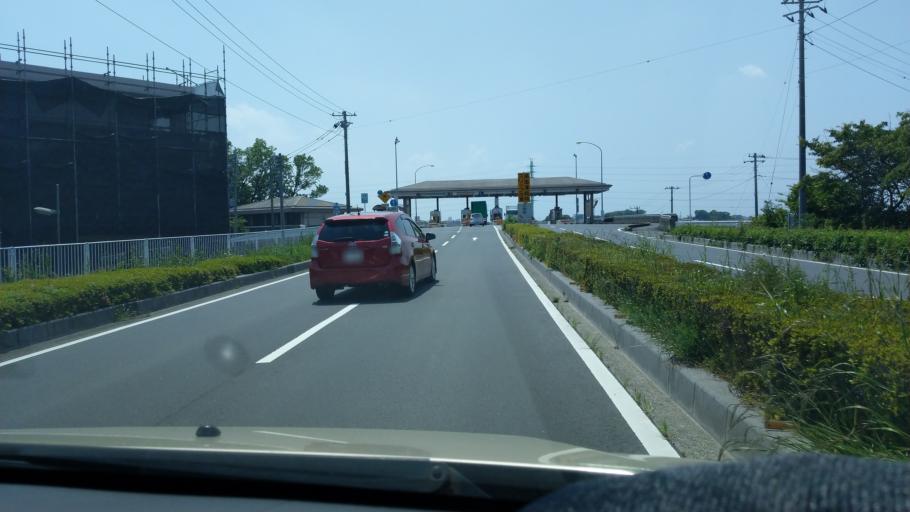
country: JP
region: Saitama
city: Saitama
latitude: 35.8876
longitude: 139.7059
